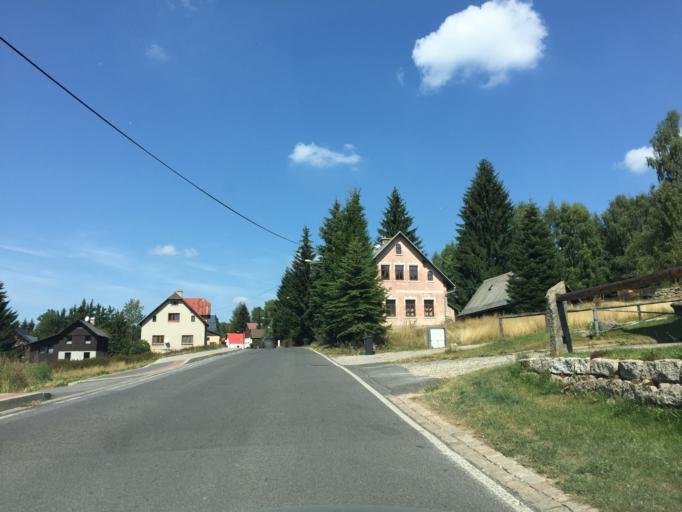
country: CZ
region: Liberecky
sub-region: Okres Jablonec nad Nisou
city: Janov nad Nisou
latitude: 50.7884
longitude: 15.1482
